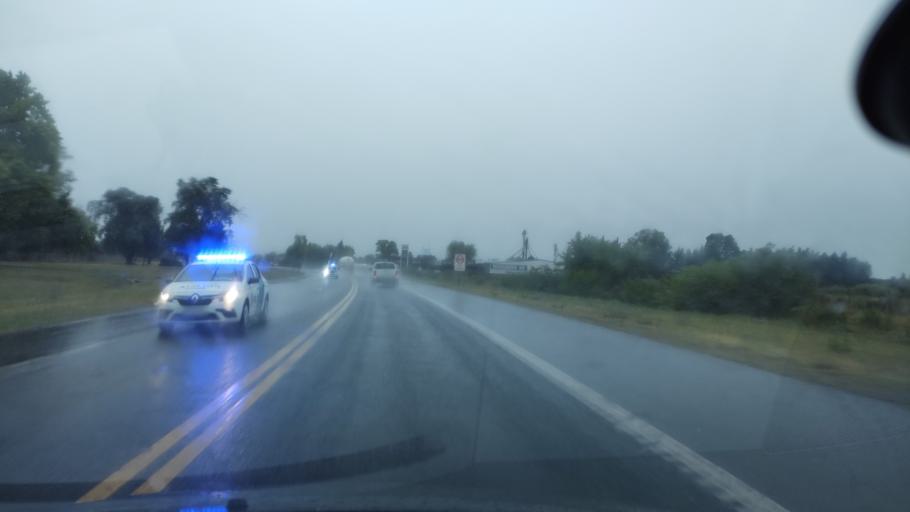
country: AR
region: Buenos Aires
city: Canuelas
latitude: -35.0524
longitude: -58.7761
